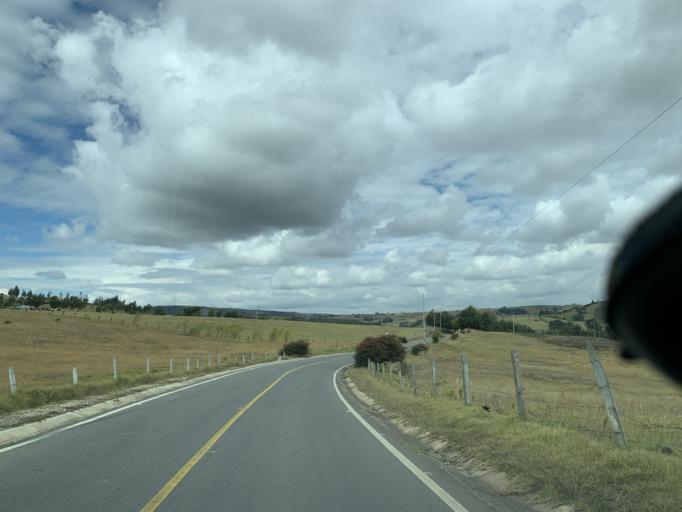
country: CO
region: Boyaca
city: Toca
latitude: 5.5694
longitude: -73.2077
